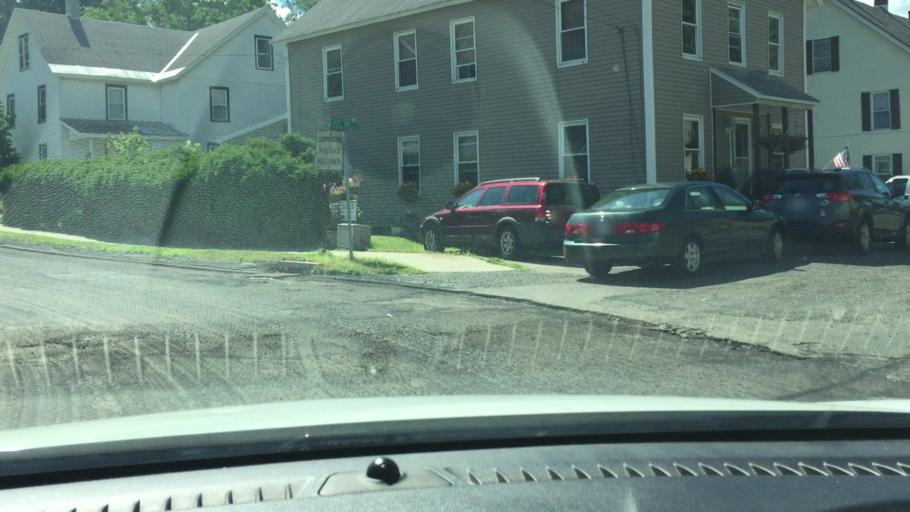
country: US
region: Massachusetts
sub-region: Berkshire County
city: Pittsfield
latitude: 42.4436
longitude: -73.2601
